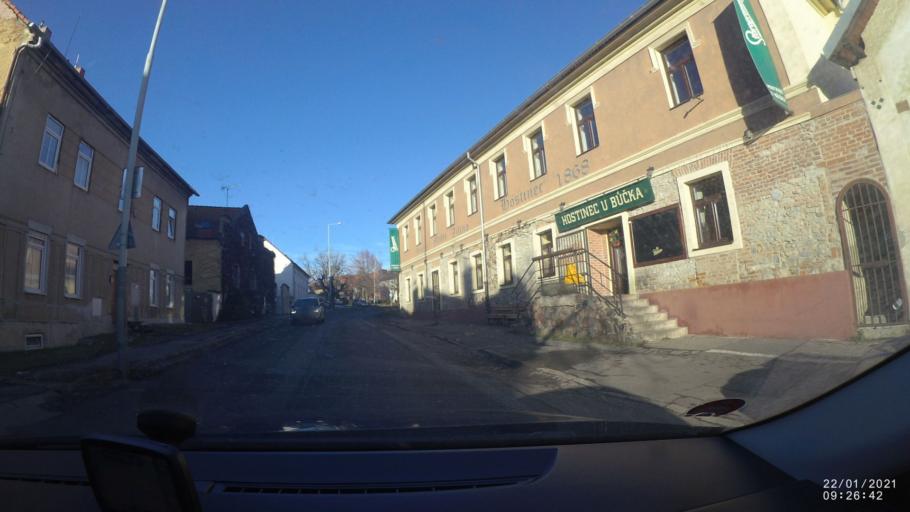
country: CZ
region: Praha
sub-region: Praha 12
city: Modrany
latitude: 50.0186
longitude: 14.3564
